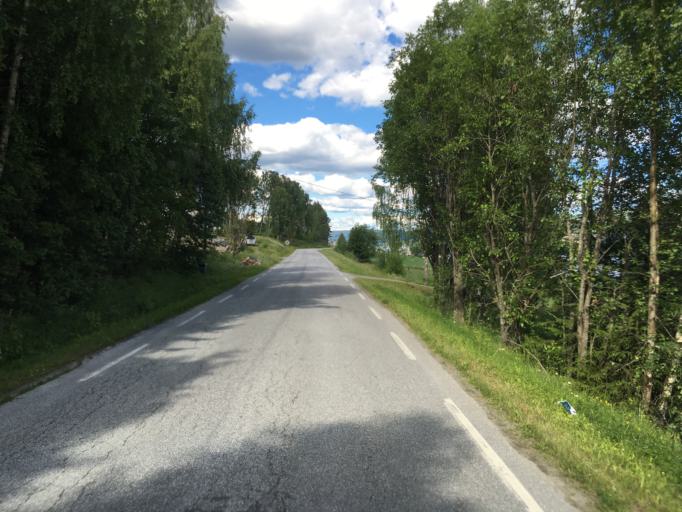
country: NO
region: Oppland
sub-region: Sondre Land
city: Hov
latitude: 60.5280
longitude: 10.2891
